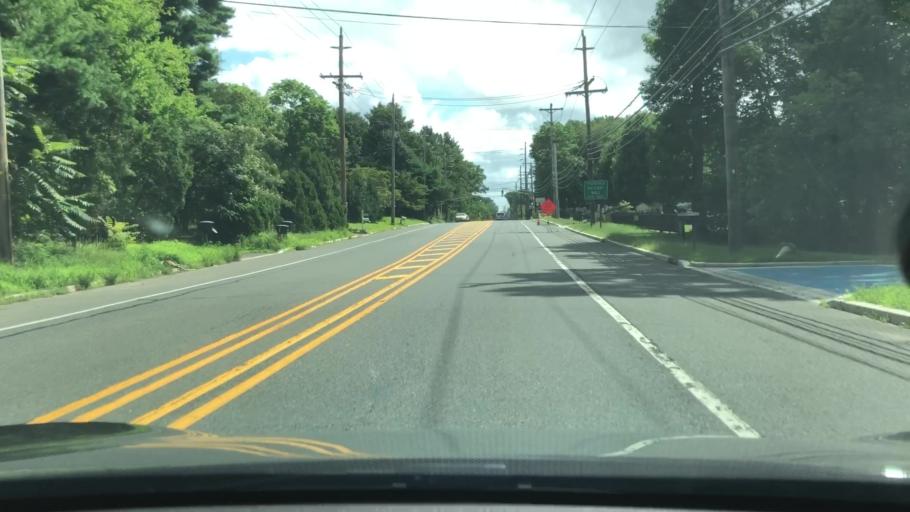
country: US
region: New Jersey
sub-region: Monmouth County
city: West Freehold
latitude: 40.2579
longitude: -74.3050
